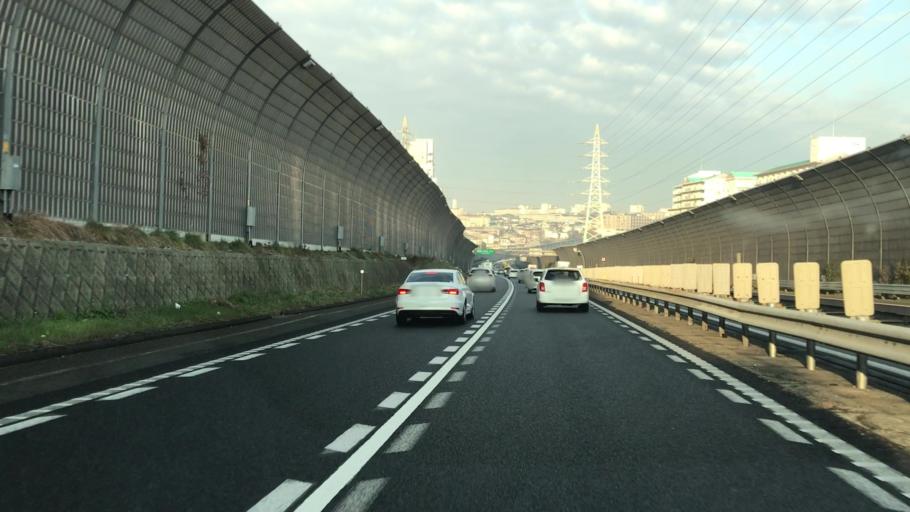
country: JP
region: Hyogo
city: Akashi
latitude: 34.6500
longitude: 135.0451
